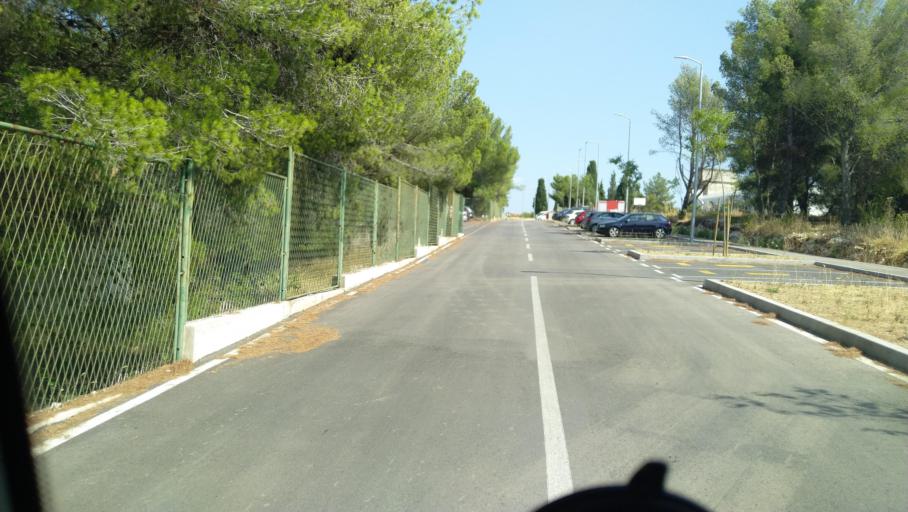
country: HR
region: Sibensko-Kniniska
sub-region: Grad Sibenik
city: Sibenik
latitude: 43.7172
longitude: 15.9072
